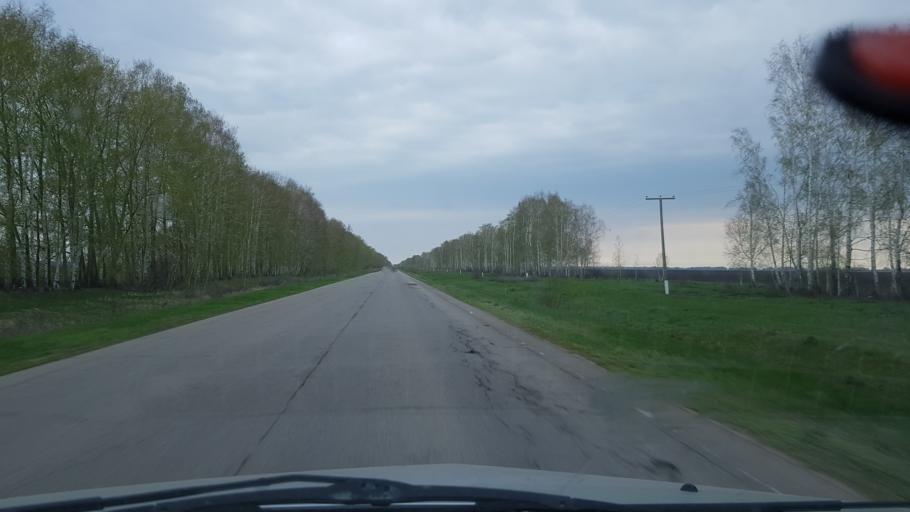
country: RU
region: Samara
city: Podstepki
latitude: 53.6598
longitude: 49.2267
